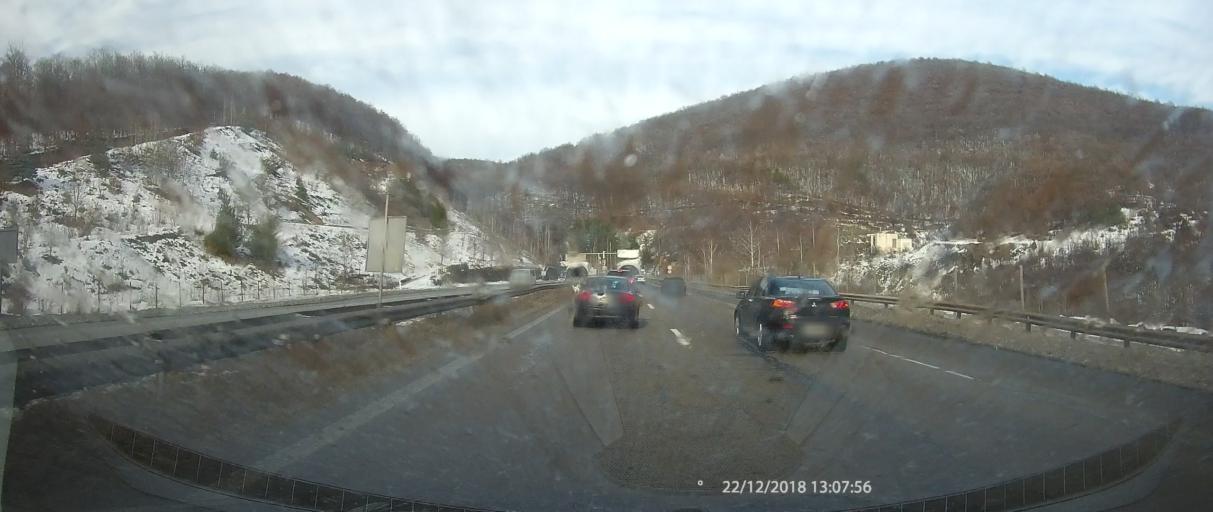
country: BG
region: Sofiya
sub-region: Obshtina Botevgrad
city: Botevgrad
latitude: 42.8301
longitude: 23.7967
